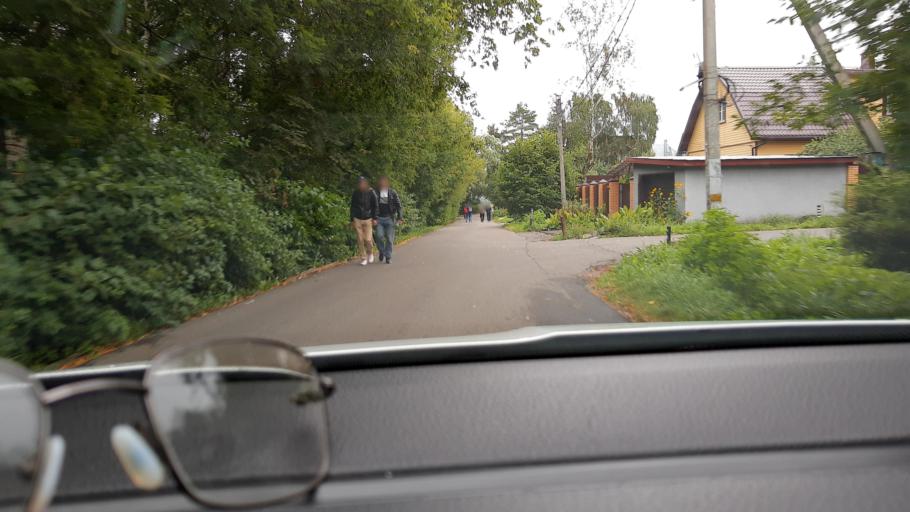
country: RU
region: Moskovskaya
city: Kokoshkino
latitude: 55.5937
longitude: 37.1731
